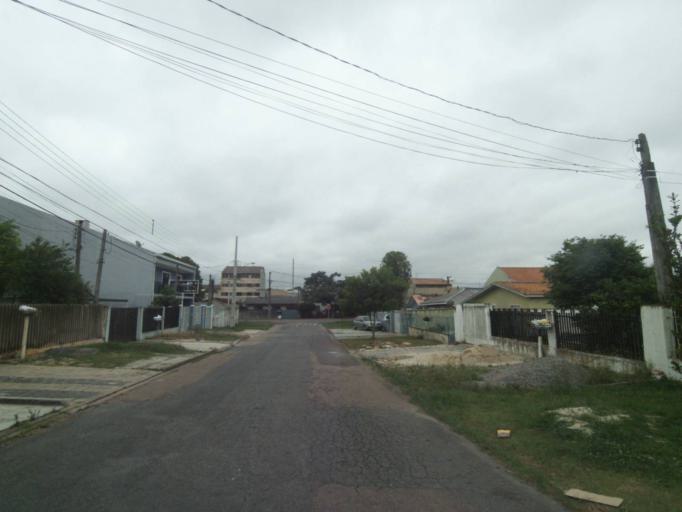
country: BR
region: Parana
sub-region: Sao Jose Dos Pinhais
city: Sao Jose dos Pinhais
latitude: -25.5452
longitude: -49.2801
